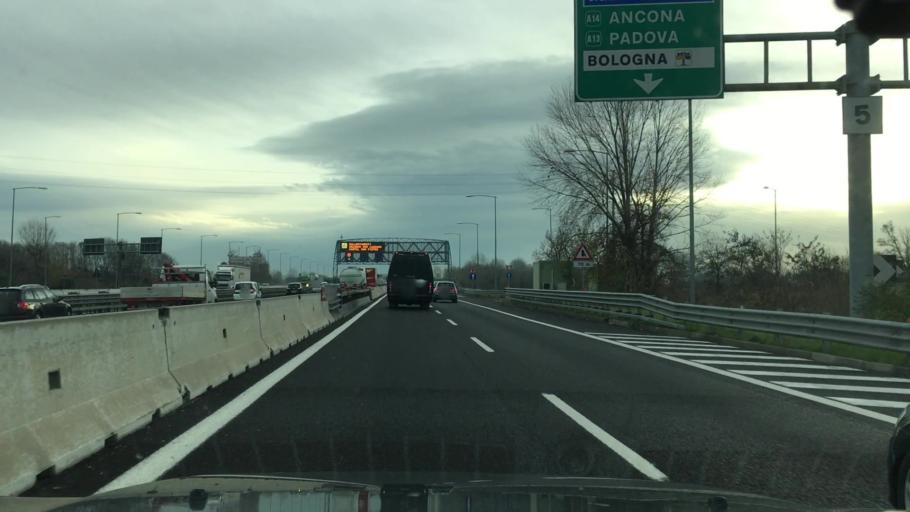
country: IT
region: Emilia-Romagna
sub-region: Provincia di Bologna
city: Trebbo
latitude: 44.5311
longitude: 11.3378
